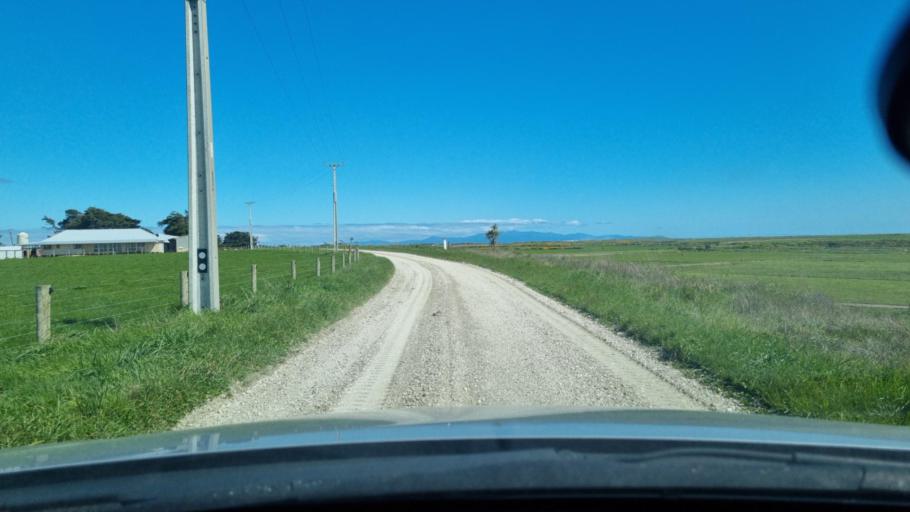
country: NZ
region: Southland
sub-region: Invercargill City
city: Invercargill
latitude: -46.3986
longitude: 168.2567
